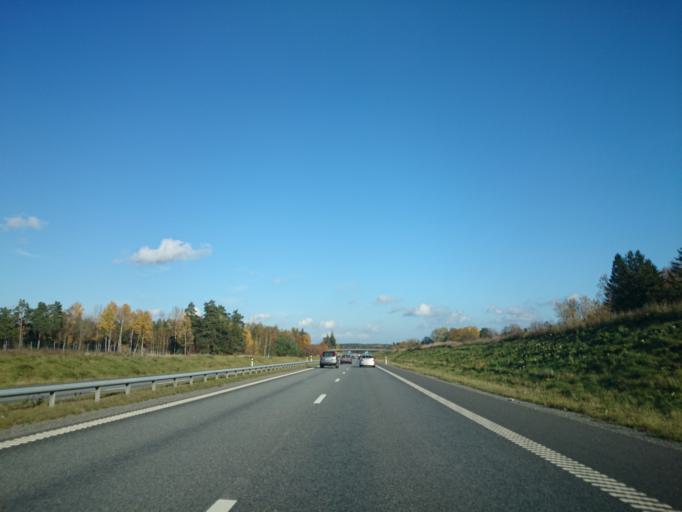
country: SE
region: Stockholm
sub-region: Haninge Kommun
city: Jordbro
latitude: 59.0924
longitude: 18.0966
